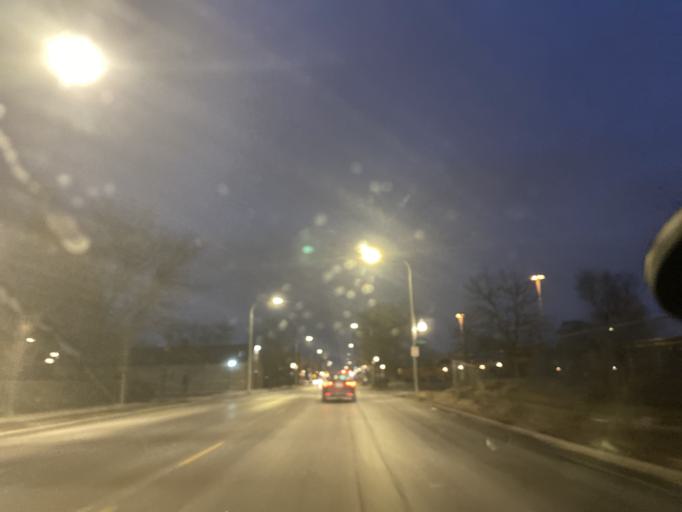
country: US
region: Illinois
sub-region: Cook County
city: Chicago
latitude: 41.7795
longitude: -87.6587
